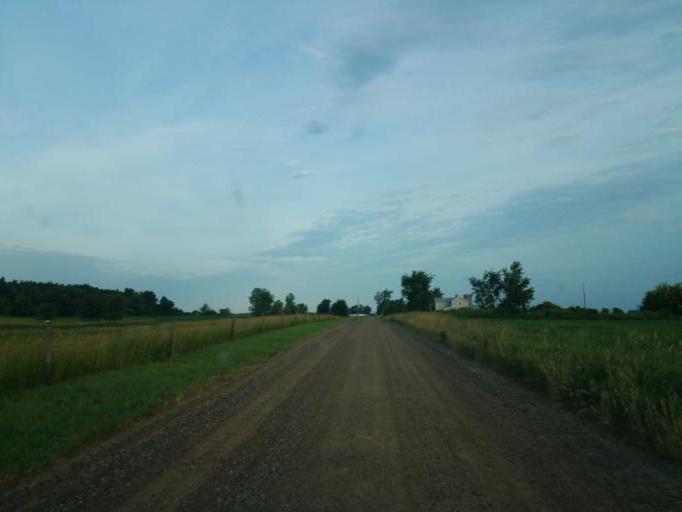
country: US
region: Michigan
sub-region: Eaton County
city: Charlotte
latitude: 42.5972
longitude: -84.9384
